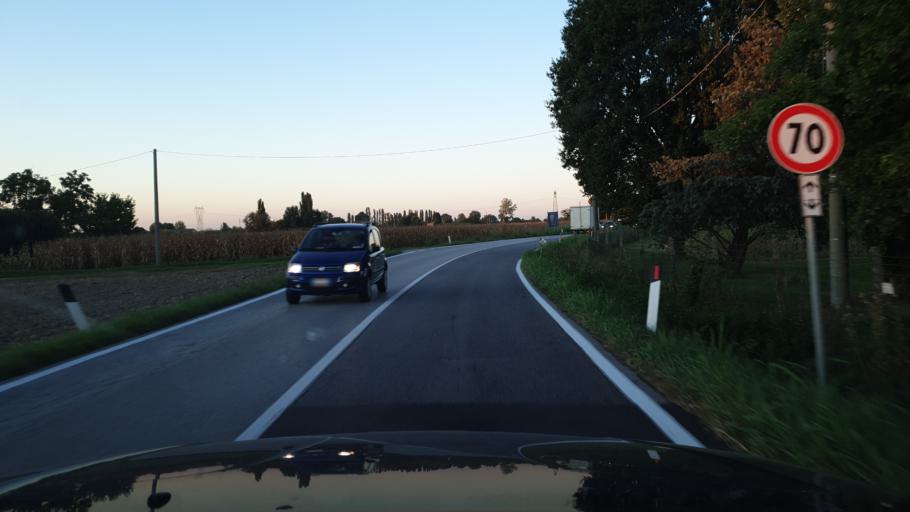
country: IT
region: Emilia-Romagna
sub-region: Provincia di Bologna
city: Progresso
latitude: 44.5661
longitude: 11.4008
